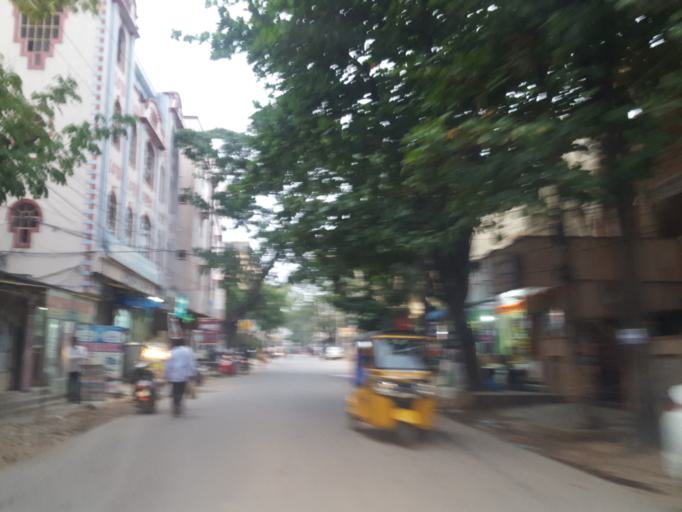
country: IN
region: Telangana
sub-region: Medak
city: Serilingampalle
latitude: 17.4940
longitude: 78.3321
